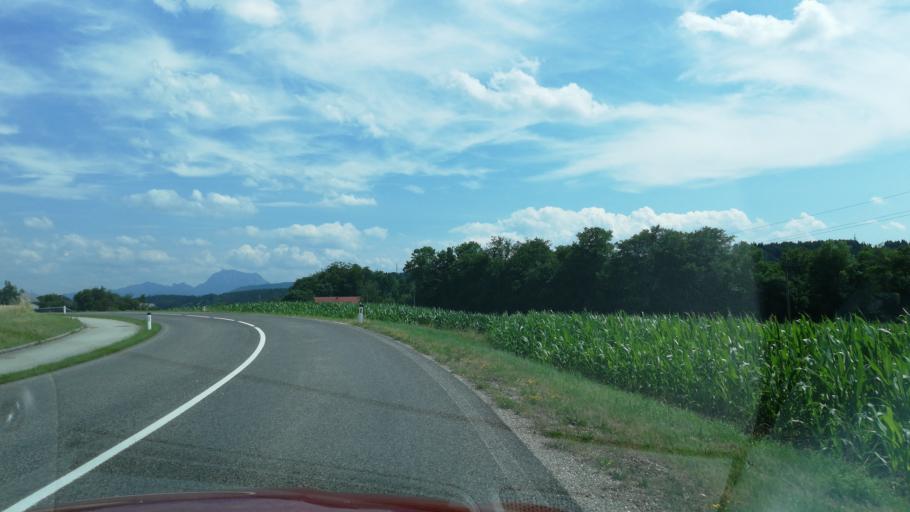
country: AT
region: Upper Austria
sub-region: Politischer Bezirk Vocklabruck
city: Timelkam
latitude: 48.0018
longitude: 13.6293
